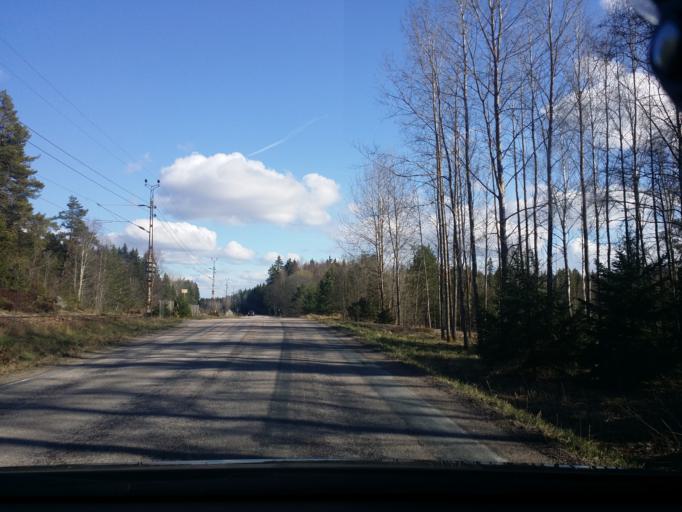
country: SE
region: Vaestmanland
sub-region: Sala Kommun
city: Sala
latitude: 59.9531
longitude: 16.5221
